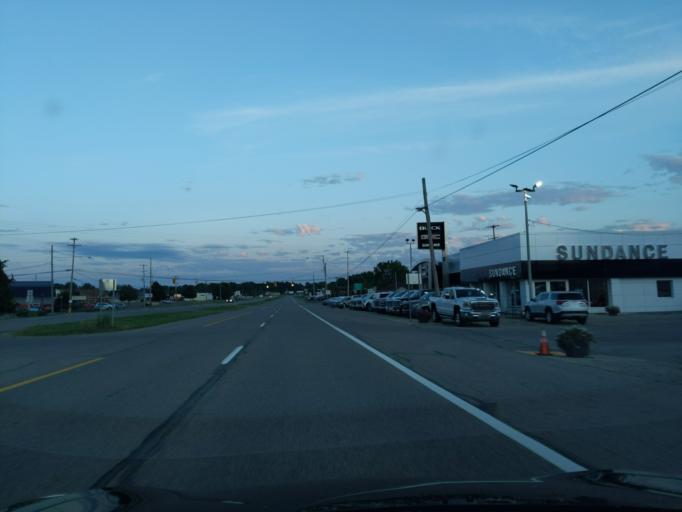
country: US
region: Michigan
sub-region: Clinton County
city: Saint Johns
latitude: 43.0151
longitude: -84.5593
